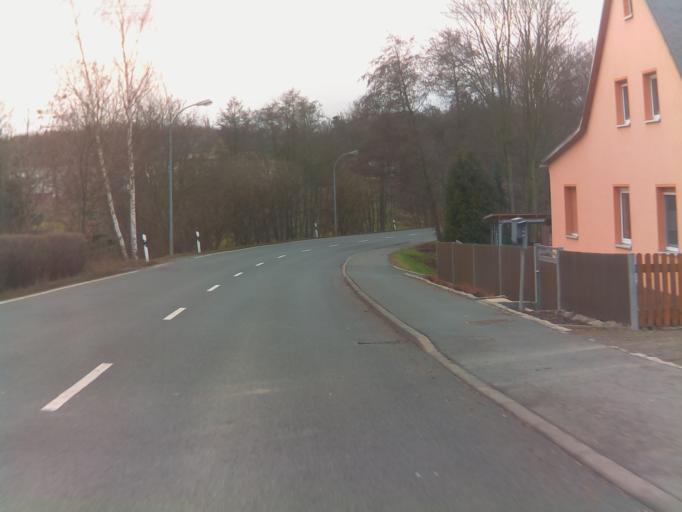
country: DE
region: Thuringia
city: Zeulenroda
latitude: 50.6421
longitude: 11.9877
